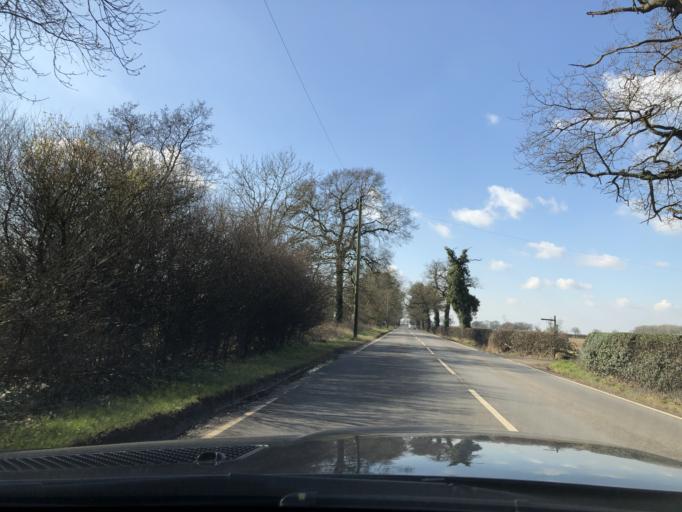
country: GB
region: England
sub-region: Warwickshire
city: Wolston
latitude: 52.3387
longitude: -1.3576
